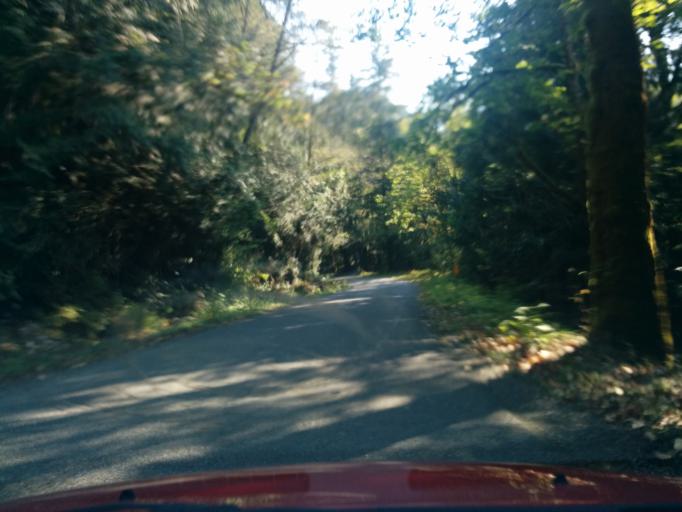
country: US
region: Washington
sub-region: Snohomish County
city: Darrington
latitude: 48.5221
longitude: -121.3739
